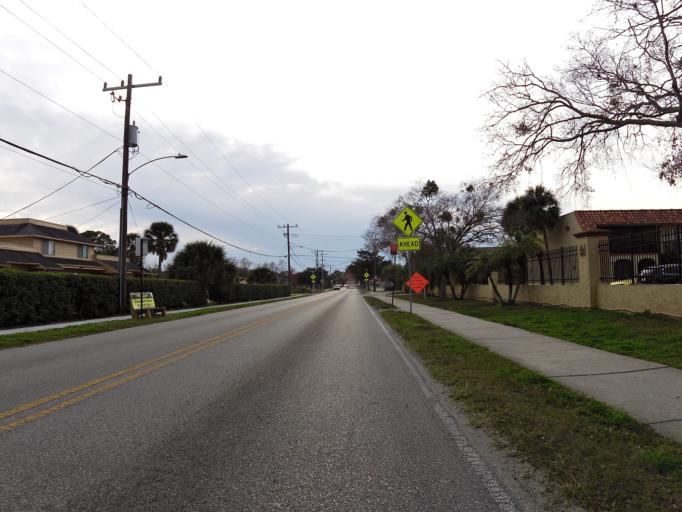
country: US
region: Florida
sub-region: Duval County
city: Jacksonville
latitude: 30.2518
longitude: -81.6180
